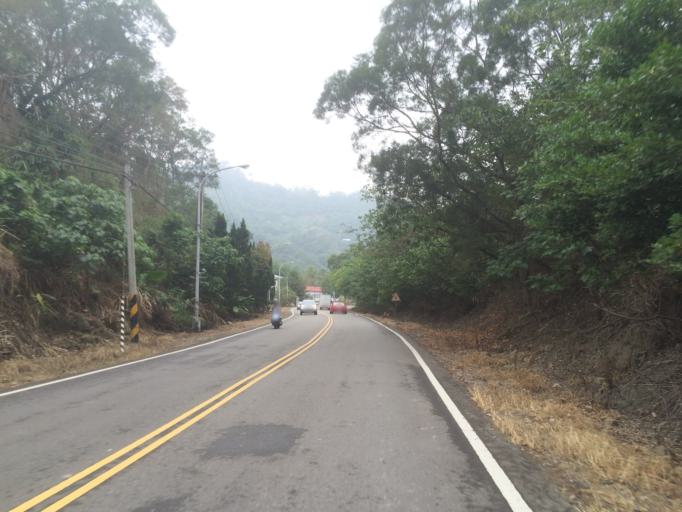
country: TW
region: Taiwan
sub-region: Taichung City
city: Taichung
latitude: 24.1601
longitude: 120.7570
